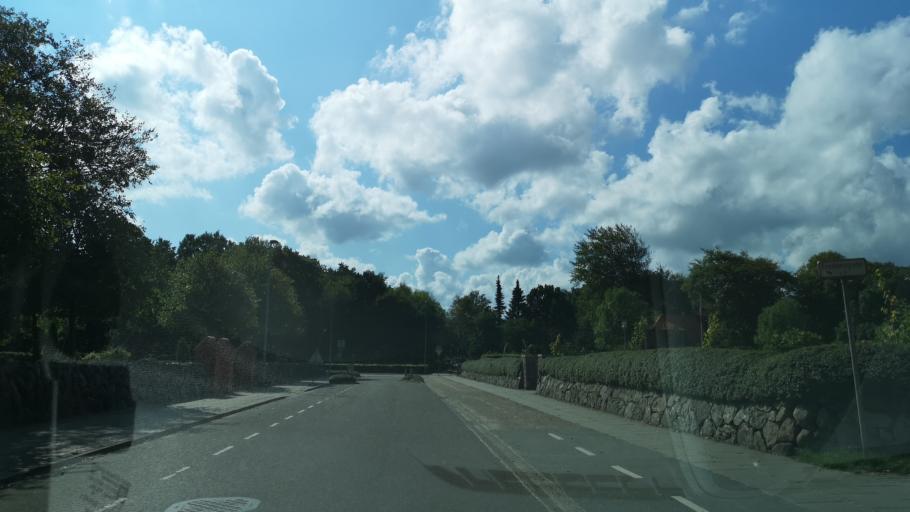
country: DK
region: Central Jutland
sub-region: Ringkobing-Skjern Kommune
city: Skjern
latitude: 55.9435
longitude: 8.5012
